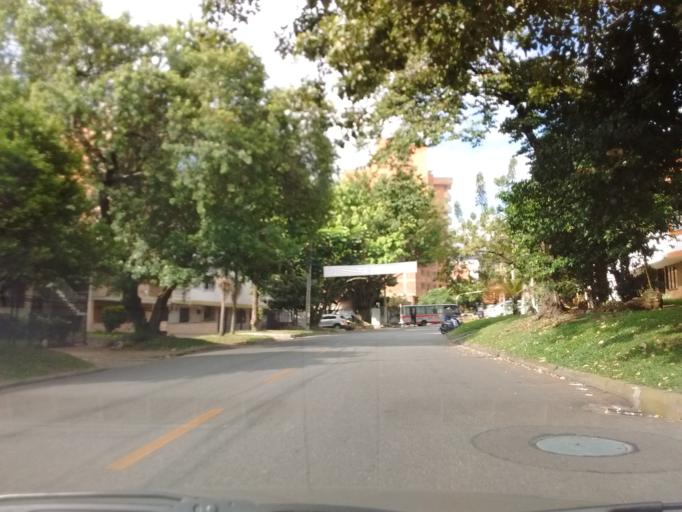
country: CO
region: Antioquia
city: Medellin
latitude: 6.2449
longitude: -75.6064
